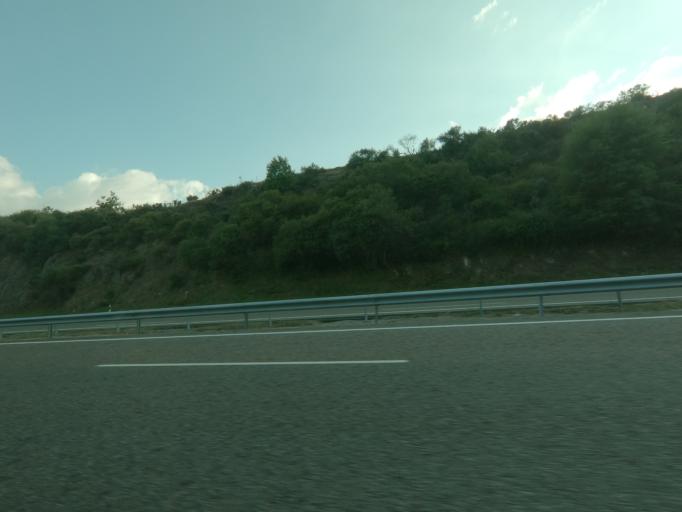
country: ES
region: Galicia
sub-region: Provincia de Ourense
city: Cualedro
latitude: 41.9931
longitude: -7.5586
